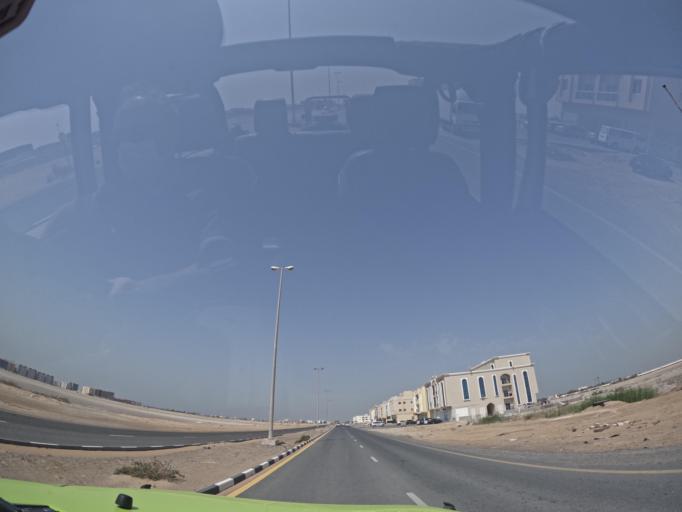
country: AE
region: Umm al Qaywayn
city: Umm al Qaywayn
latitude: 25.5151
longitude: 55.5564
